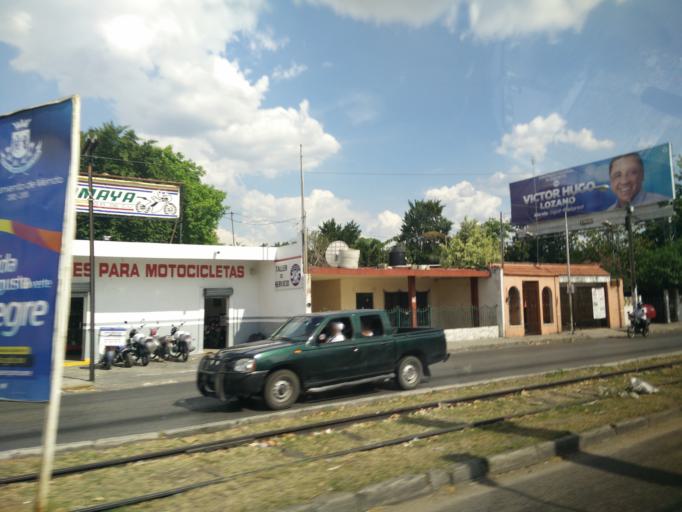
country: MX
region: Yucatan
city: Merida
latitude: 20.9653
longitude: -89.5915
